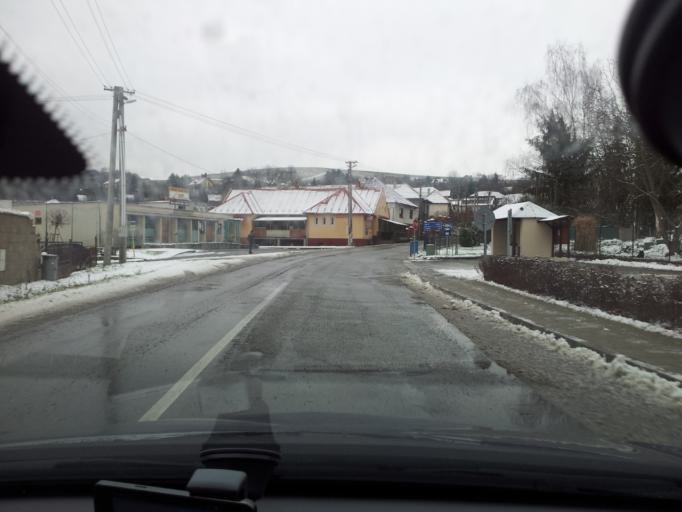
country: SK
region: Presovsky
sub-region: Okres Presov
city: Presov
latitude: 48.8611
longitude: 21.2344
